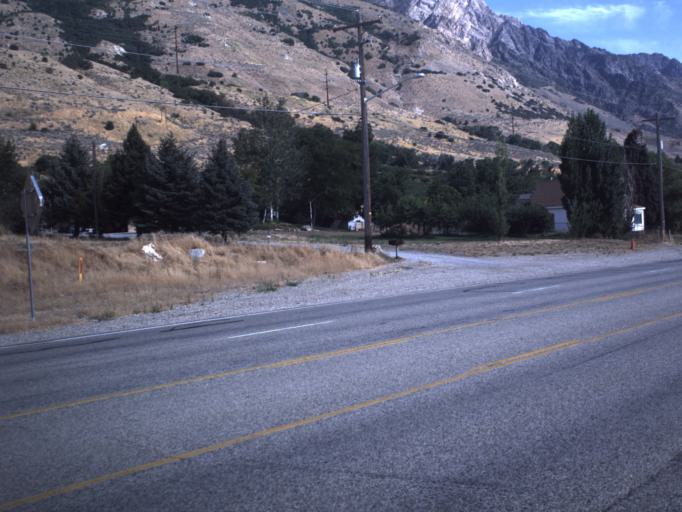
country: US
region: Utah
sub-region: Box Elder County
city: Willard
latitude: 41.4368
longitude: -112.0363
